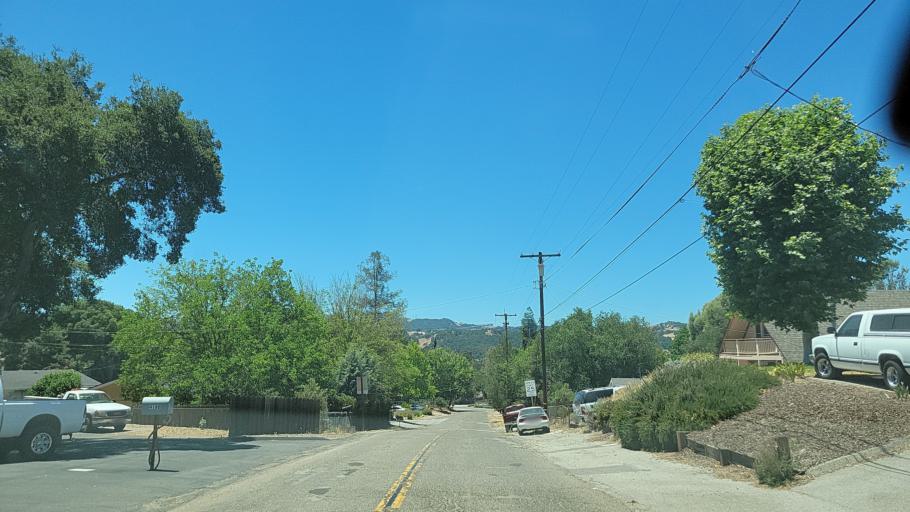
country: US
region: California
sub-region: San Luis Obispo County
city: Atascadero
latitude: 35.5058
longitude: -120.6792
